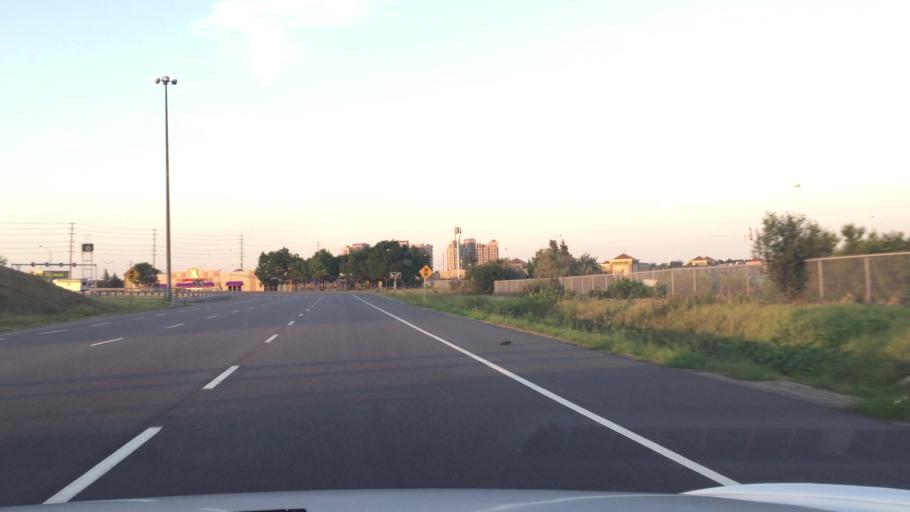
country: CA
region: Ontario
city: Vaughan
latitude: 43.8268
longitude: -79.5442
